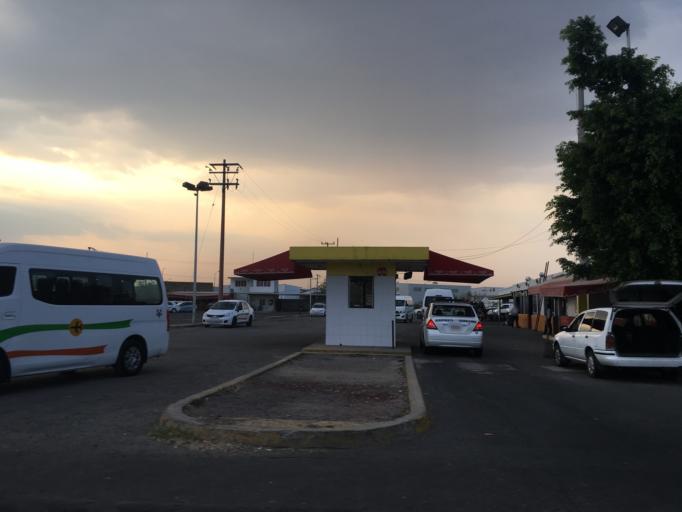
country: MX
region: Jalisco
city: El Quince
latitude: 20.5273
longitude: -103.3023
